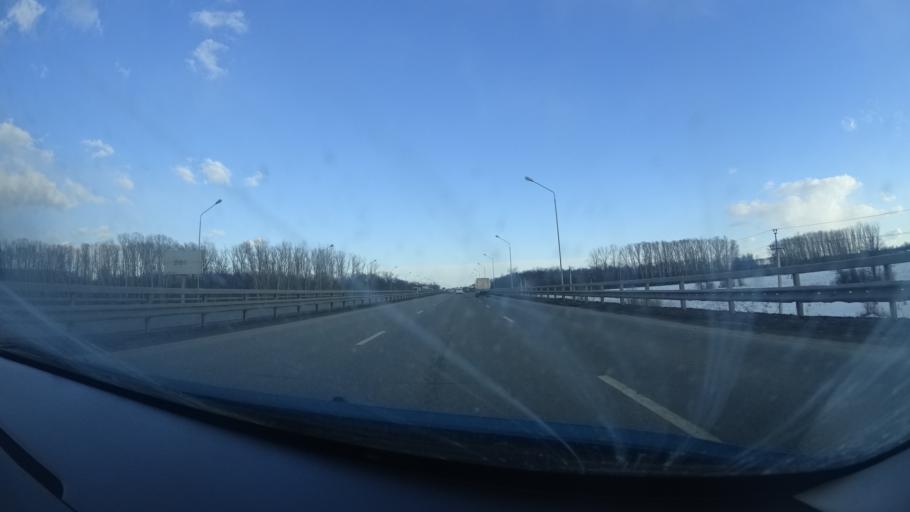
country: RU
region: Bashkortostan
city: Ufa
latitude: 54.6559
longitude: 55.8950
